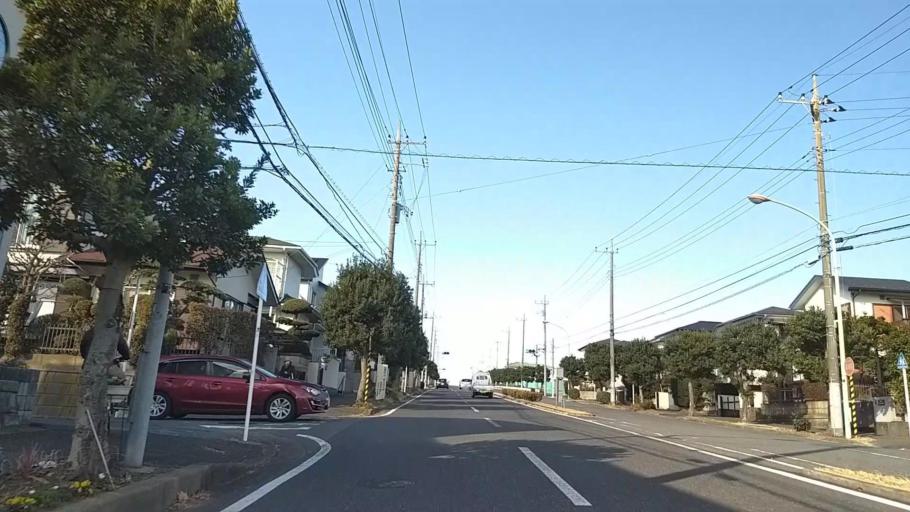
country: JP
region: Kanagawa
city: Atsugi
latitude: 35.4361
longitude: 139.3304
